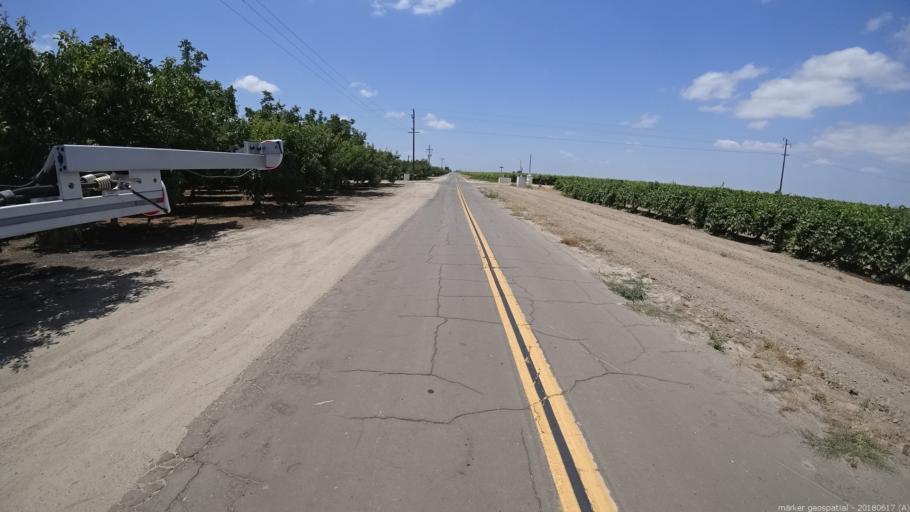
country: US
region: California
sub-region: Fresno County
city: Biola
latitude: 36.8223
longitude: -120.1141
